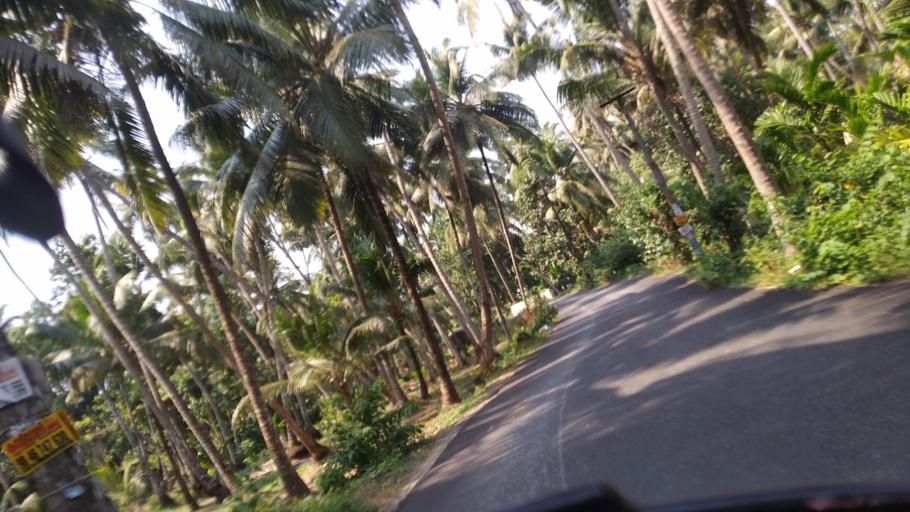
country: IN
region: Kerala
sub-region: Thrissur District
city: Thanniyam
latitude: 10.3574
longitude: 76.1100
